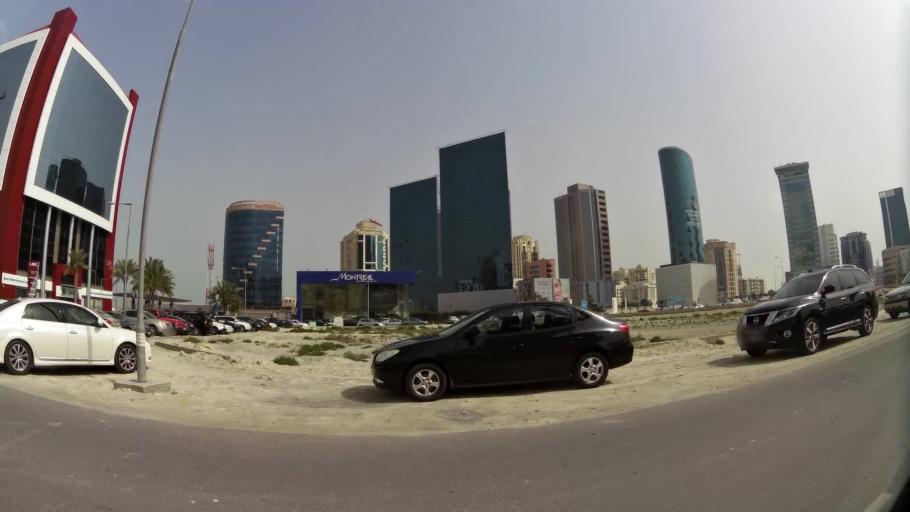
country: BH
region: Manama
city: Jidd Hafs
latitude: 26.2373
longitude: 50.5339
